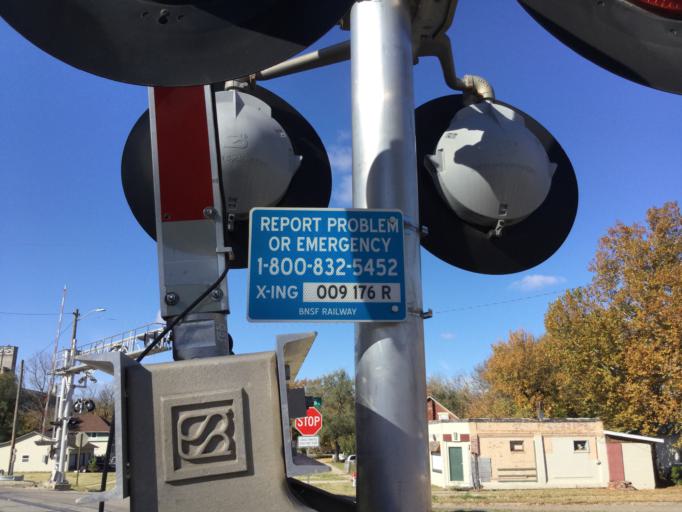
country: US
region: Kansas
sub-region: Harvey County
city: Newton
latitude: 38.0524
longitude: -97.3350
